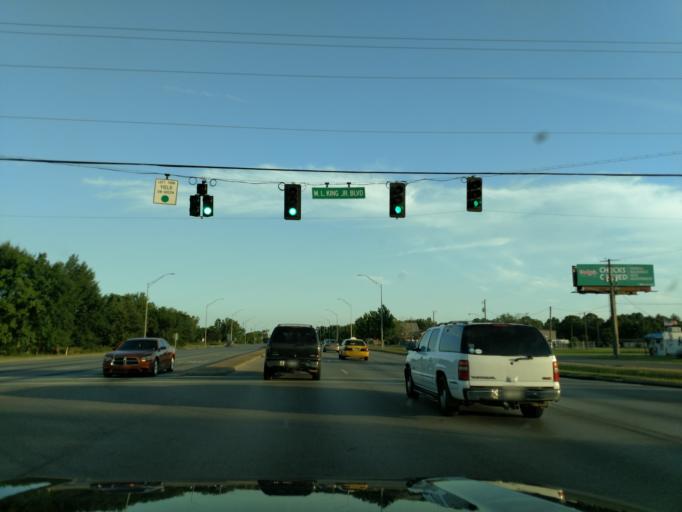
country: US
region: Mississippi
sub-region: Harrison County
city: West Gulfport
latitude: 30.4041
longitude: -89.0929
